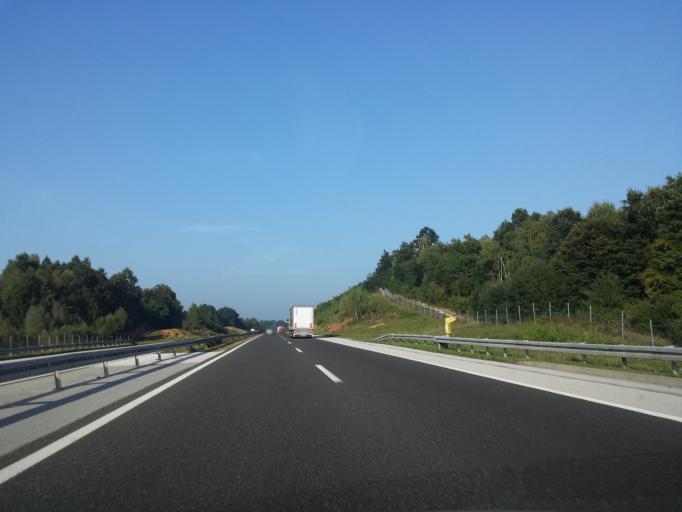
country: SI
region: Crnomelj
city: Crnomelj
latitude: 45.4348
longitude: 15.3272
